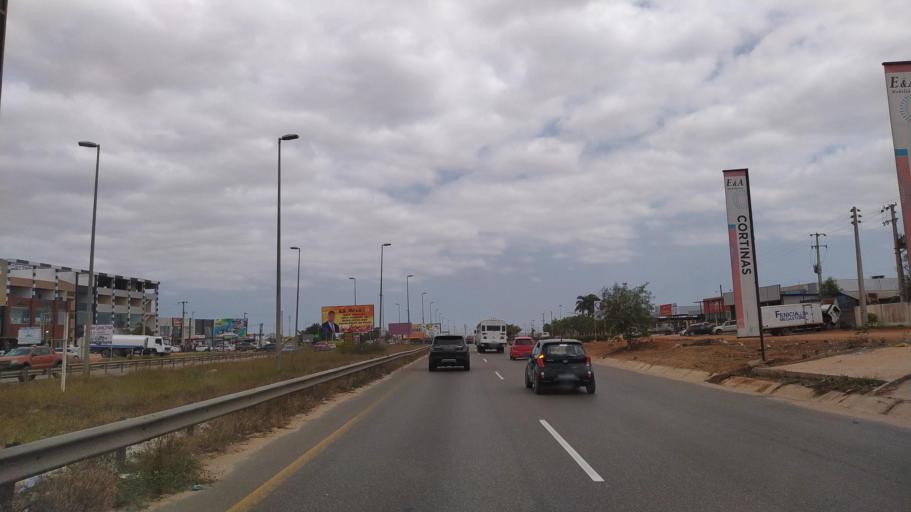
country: AO
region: Luanda
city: Luanda
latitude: -8.9793
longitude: 13.1921
